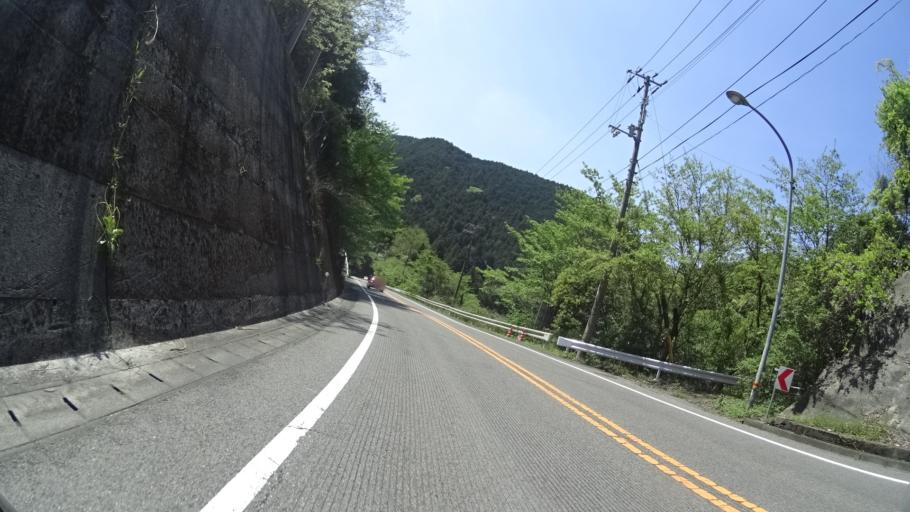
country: JP
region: Ehime
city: Hojo
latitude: 33.9561
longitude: 132.9114
